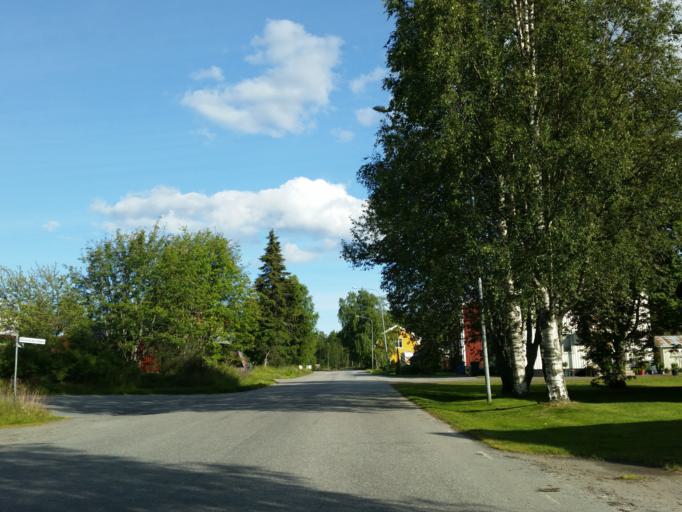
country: SE
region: Vaesterbotten
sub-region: Robertsfors Kommun
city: Robertsfors
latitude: 64.0599
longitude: 20.8517
